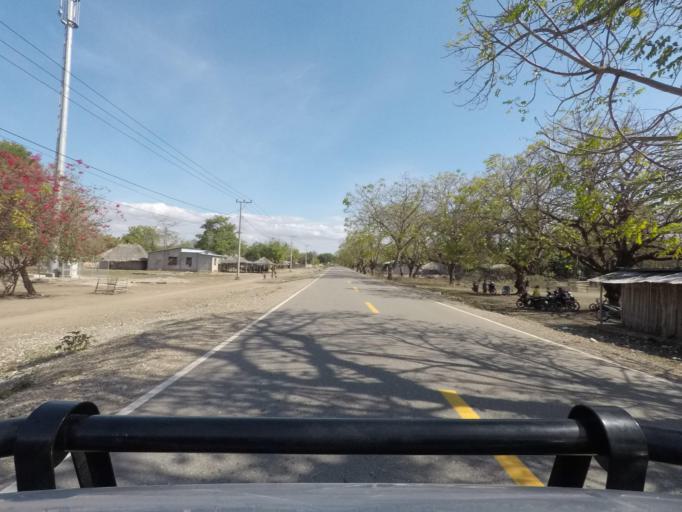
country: ID
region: East Nusa Tenggara
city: Atambua
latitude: -8.9025
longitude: 124.9981
